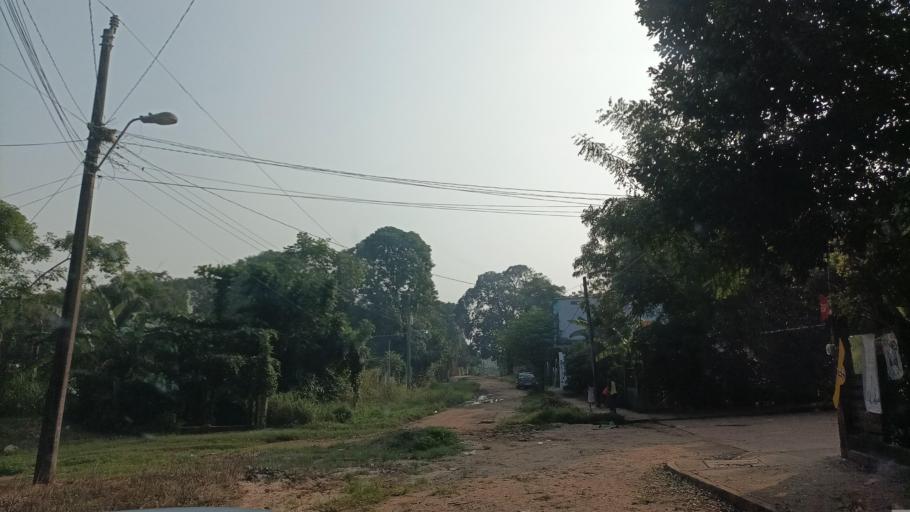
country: MX
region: Veracruz
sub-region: Cosoleacaque
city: Residencial las Olas
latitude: 18.0968
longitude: -94.5711
